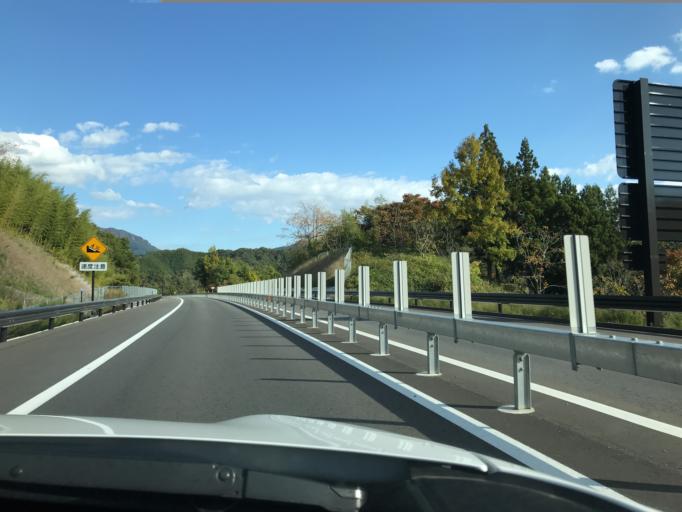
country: JP
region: Fukushima
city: Hobaramachi
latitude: 37.7580
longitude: 140.6024
